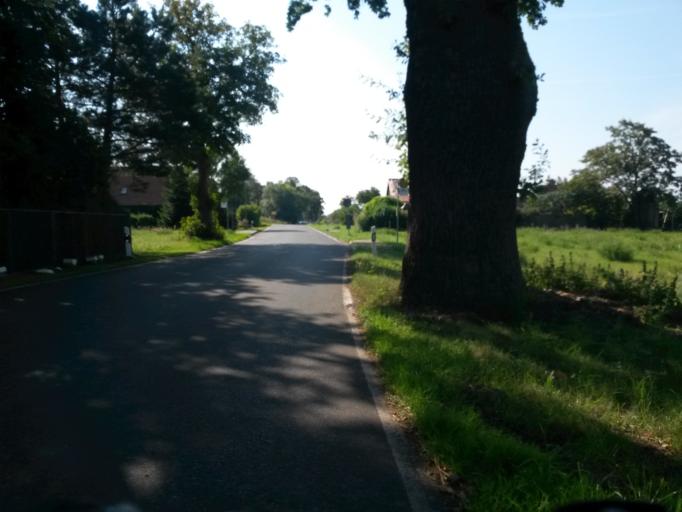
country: DE
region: Brandenburg
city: Templin
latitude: 53.0687
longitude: 13.4339
